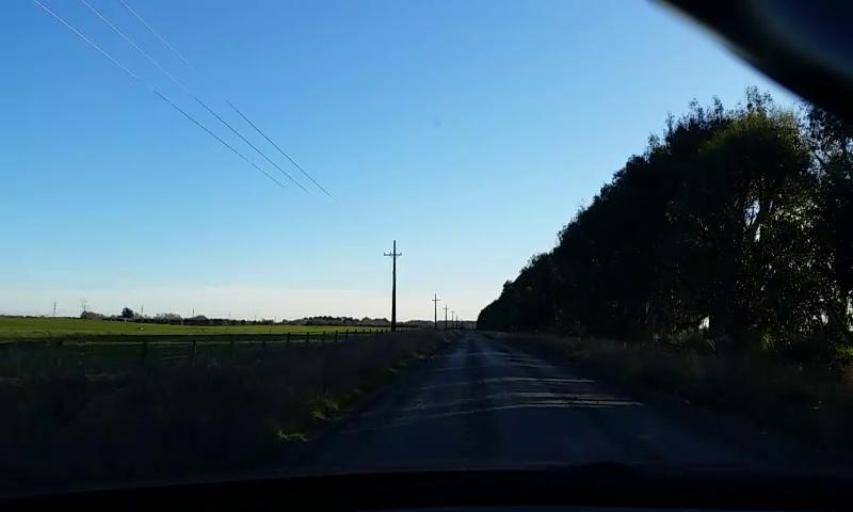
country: NZ
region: Southland
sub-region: Invercargill City
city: Invercargill
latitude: -46.2918
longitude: 168.4462
